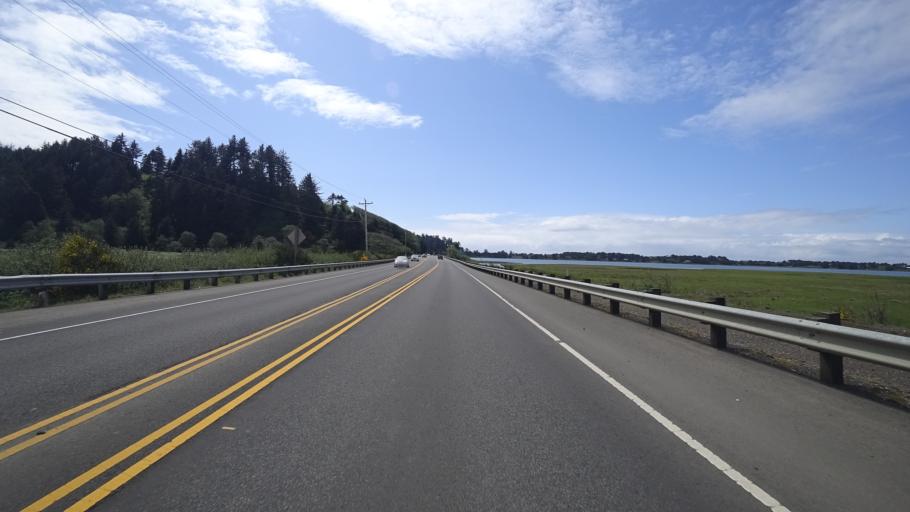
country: US
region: Oregon
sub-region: Lincoln County
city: Lincoln Beach
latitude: 44.8939
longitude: -124.0155
